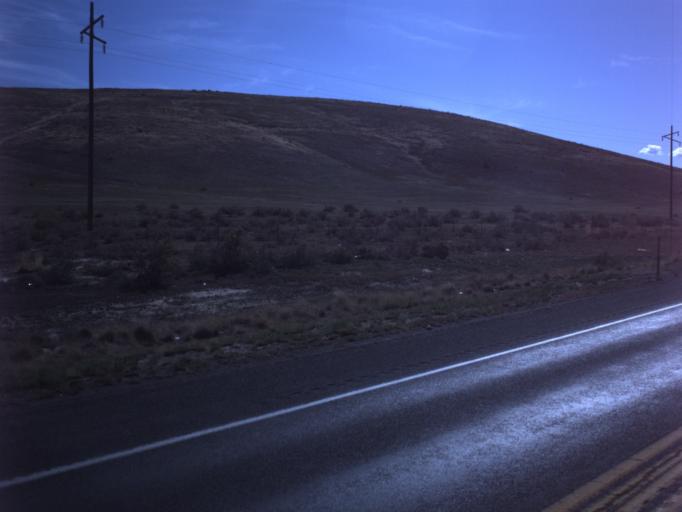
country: US
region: Utah
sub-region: Sanpete County
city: Gunnison
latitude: 39.2057
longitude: -111.8480
